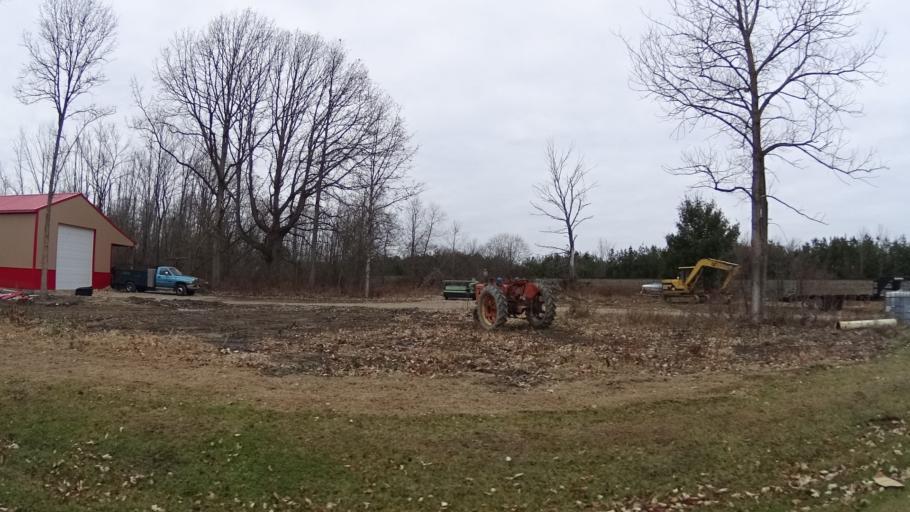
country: US
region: Ohio
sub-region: Lorain County
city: Wellington
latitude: 41.1400
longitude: -82.2692
